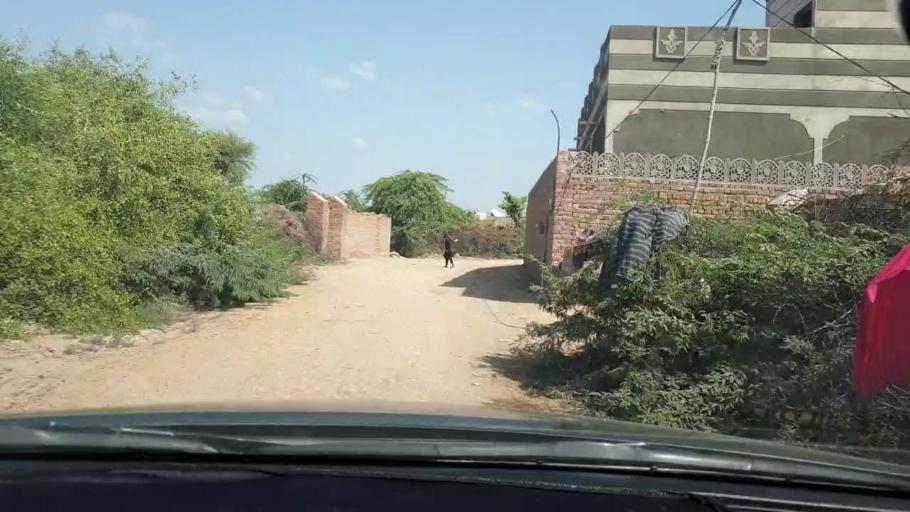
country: PK
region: Sindh
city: Naukot
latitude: 24.8776
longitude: 69.2548
